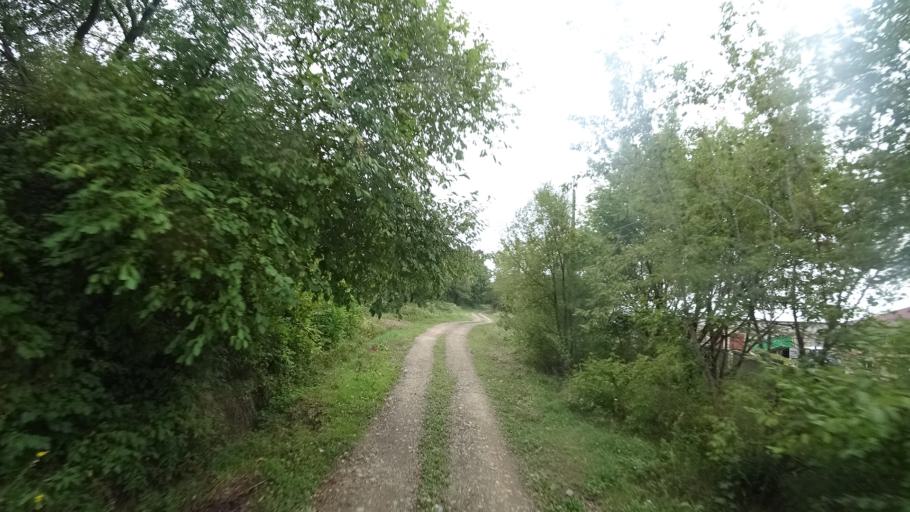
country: RU
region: Primorskiy
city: Monastyrishche
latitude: 44.2677
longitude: 132.4571
